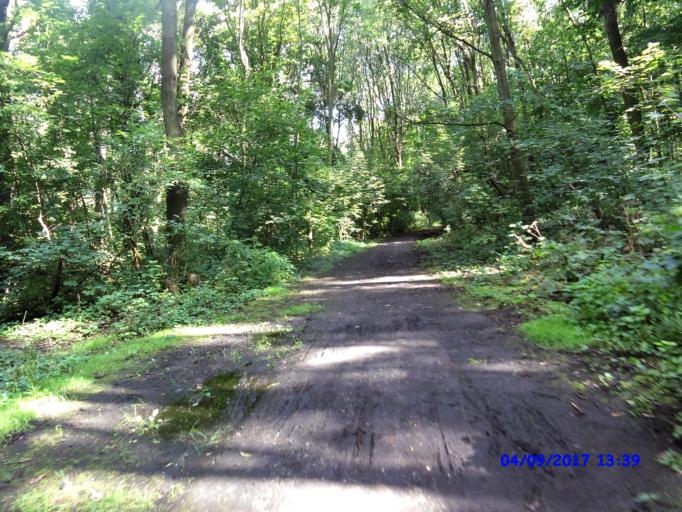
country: DE
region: Saxony
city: Taucha
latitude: 51.3550
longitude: 12.4691
